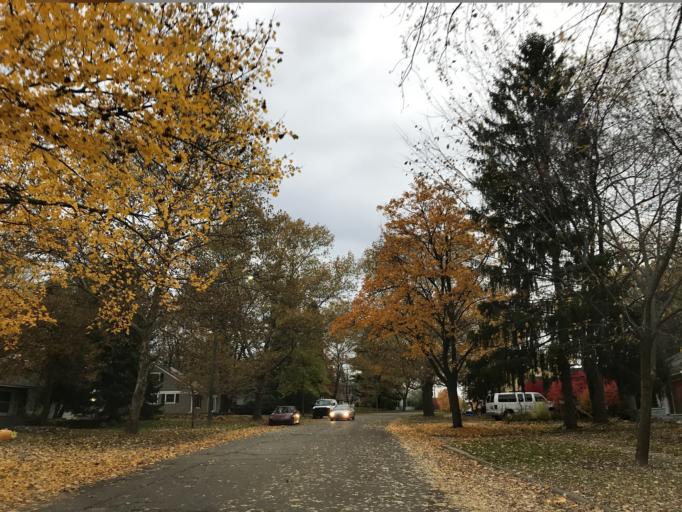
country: US
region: Michigan
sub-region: Washtenaw County
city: Ann Arbor
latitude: 42.2527
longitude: -83.6889
